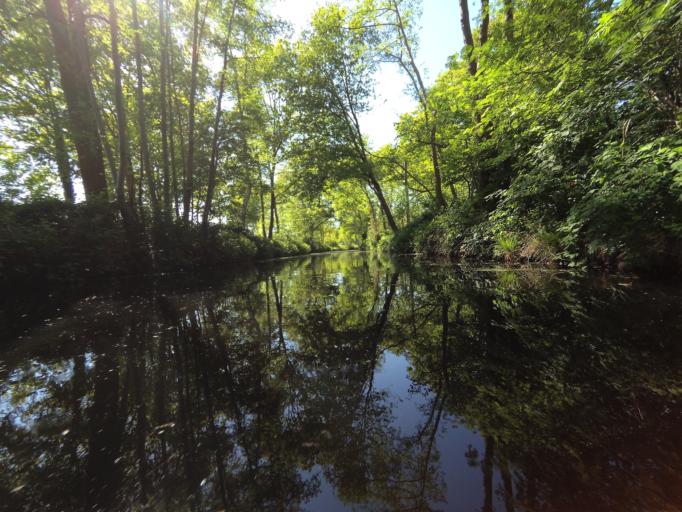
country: NL
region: Utrecht
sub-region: Gemeente Woudenberg
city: Woudenberg
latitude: 52.0965
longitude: 5.4274
